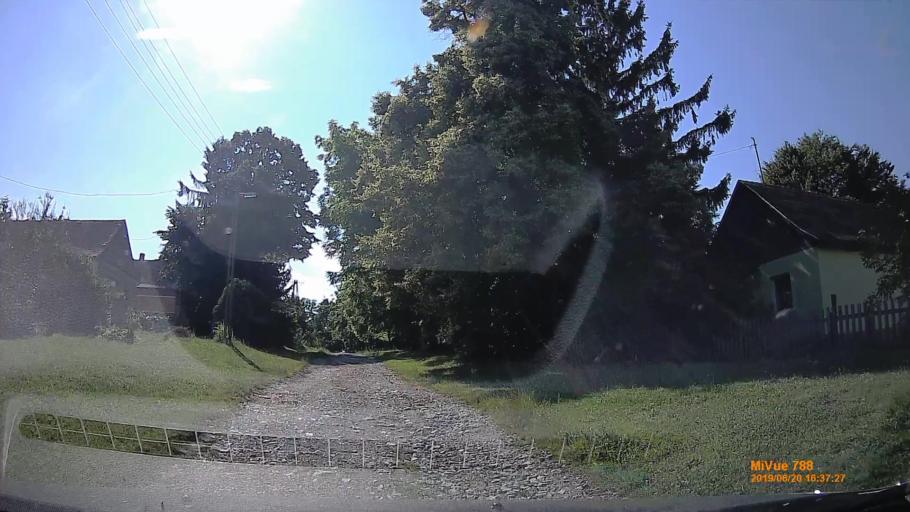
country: HU
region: Baranya
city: Buekkoesd
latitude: 46.1716
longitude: 18.0340
